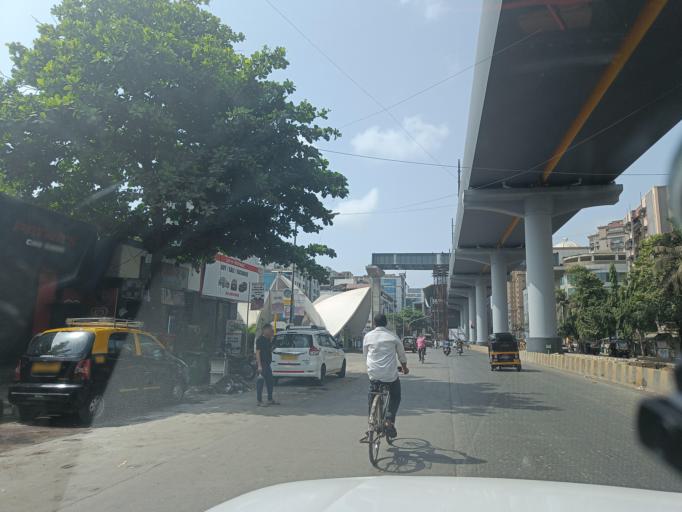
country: IN
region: Maharashtra
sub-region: Mumbai Suburban
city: Powai
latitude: 19.1427
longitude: 72.8314
